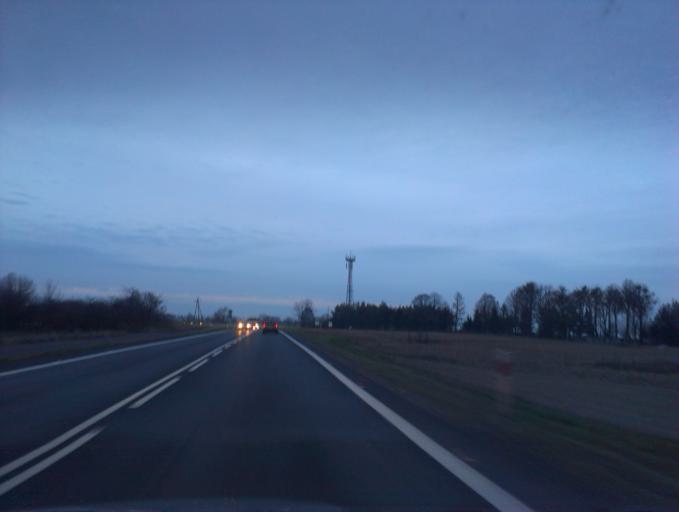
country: PL
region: Greater Poland Voivodeship
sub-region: Powiat poznanski
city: Zlotniki
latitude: 52.5652
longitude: 16.8348
